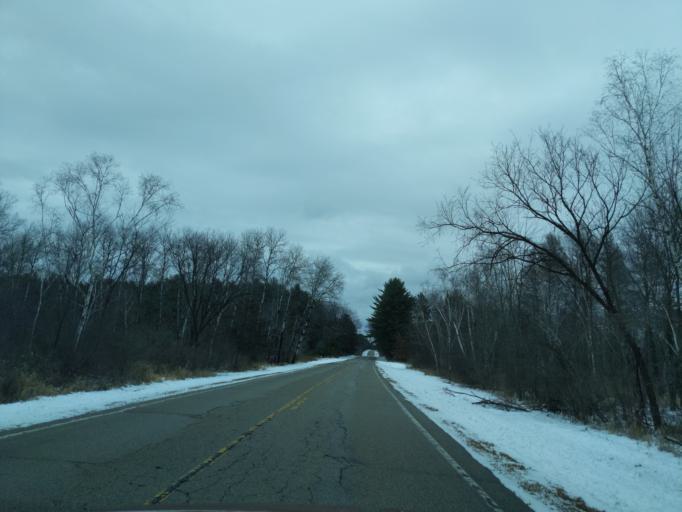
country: US
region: Wisconsin
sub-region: Marquette County
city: Montello
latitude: 43.9196
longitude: -89.3244
